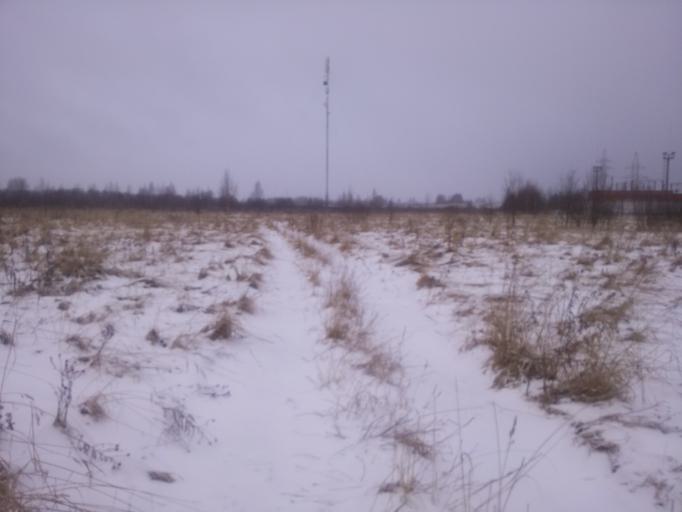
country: RU
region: Tverskaya
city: Likhoslavl'
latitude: 57.0629
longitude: 35.5592
